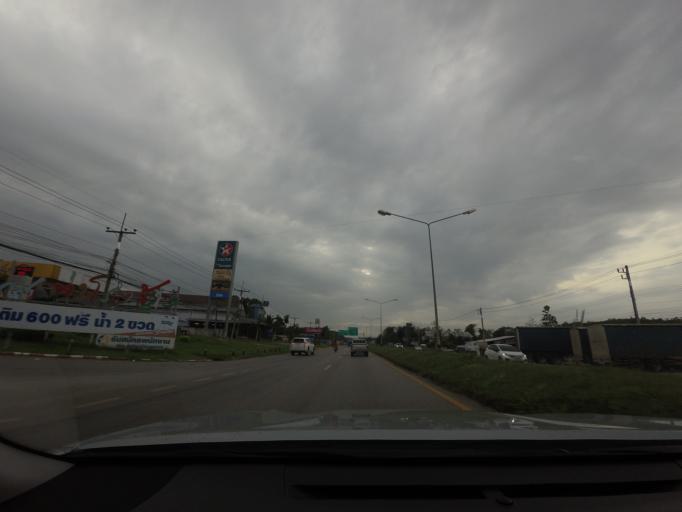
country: TH
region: Surat Thani
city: Phunphin
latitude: 9.0510
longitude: 99.1654
